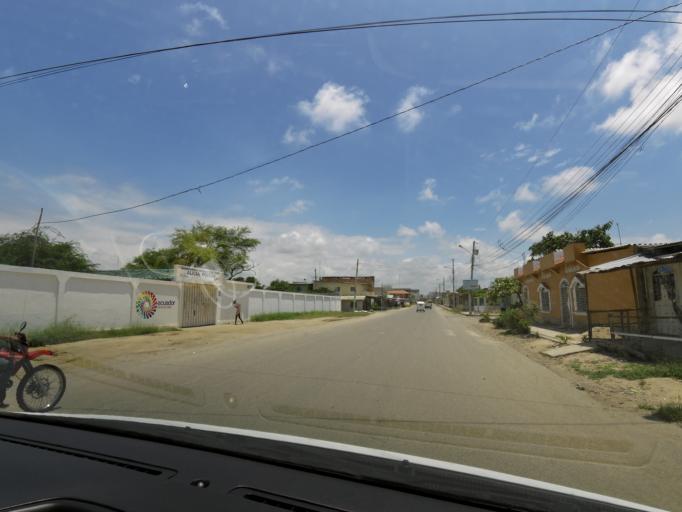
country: EC
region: El Oro
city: Huaquillas
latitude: -3.4754
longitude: -80.2361
